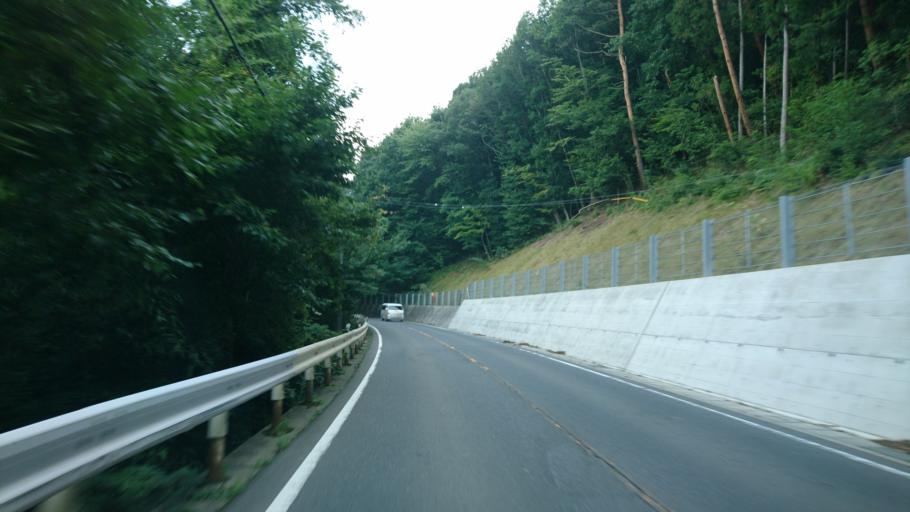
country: JP
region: Gunma
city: Numata
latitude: 36.7207
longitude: 139.2158
